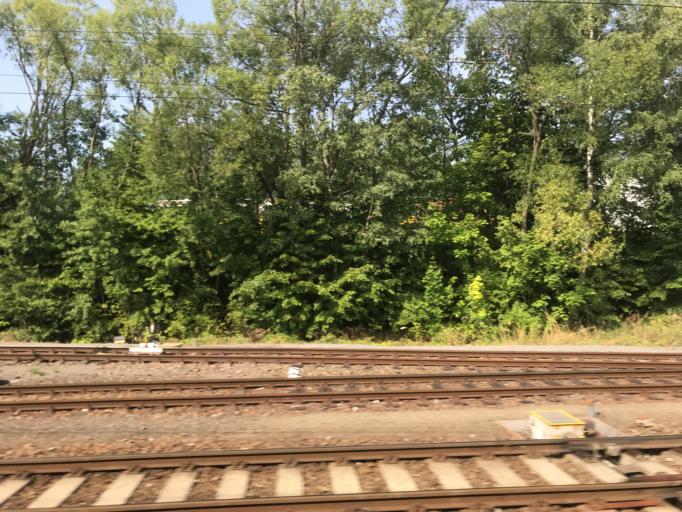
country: CZ
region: Central Bohemia
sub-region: Okres Benesov
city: Benesov
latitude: 49.7739
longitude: 14.6860
